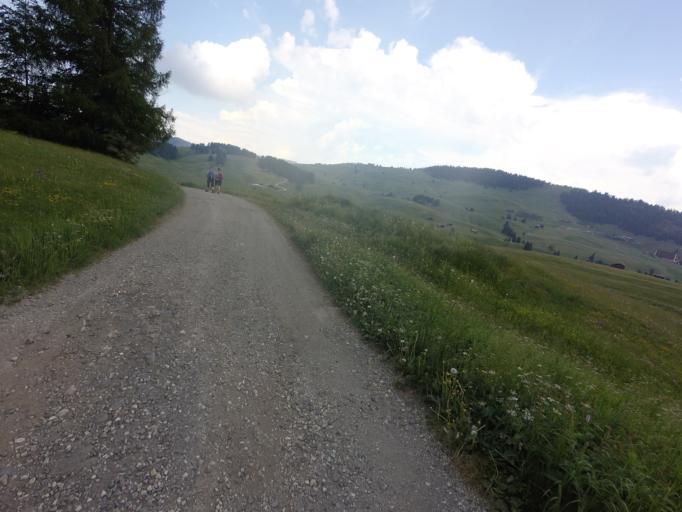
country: IT
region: Trentino-Alto Adige
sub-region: Bolzano
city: Ortisei
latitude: 46.5451
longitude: 11.6620
